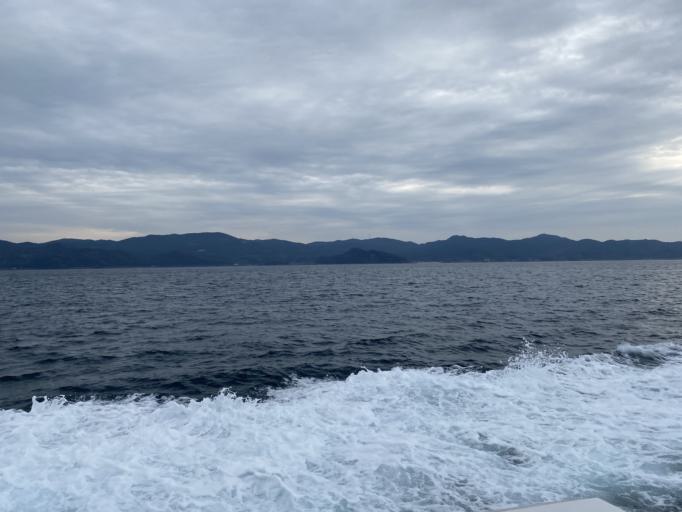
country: JP
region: Nagasaki
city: Nagasaki-shi
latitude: 32.6364
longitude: 129.7592
